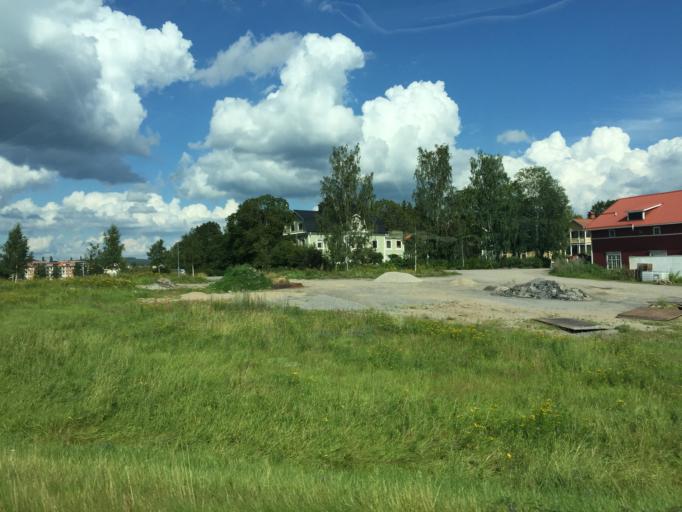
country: SE
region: Gaevleborg
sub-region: Bollnas Kommun
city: Bollnas
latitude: 61.3416
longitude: 16.3927
